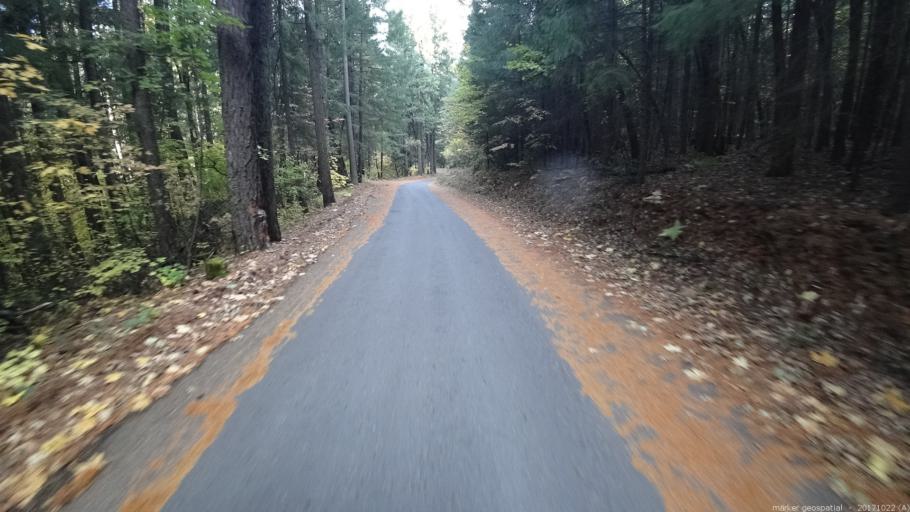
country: US
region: California
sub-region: Siskiyou County
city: Dunsmuir
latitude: 41.1603
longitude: -122.2911
